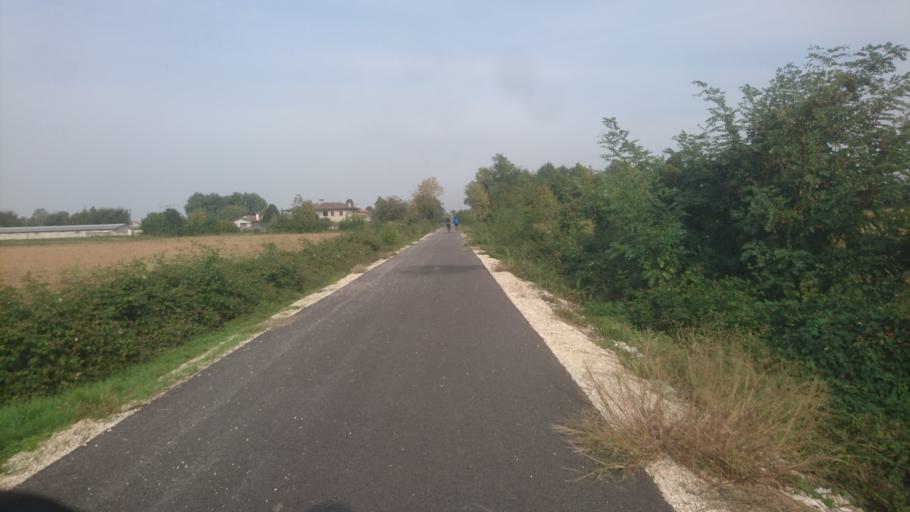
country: IT
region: Veneto
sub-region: Provincia di Vicenza
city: Montegalda
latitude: 45.4629
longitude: 11.6490
